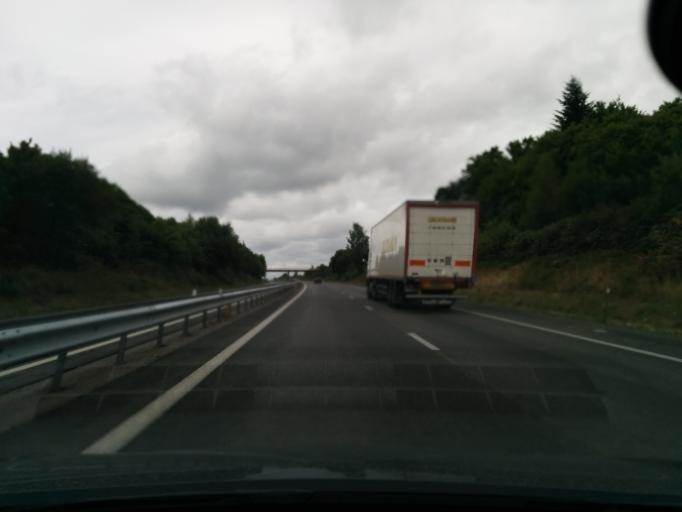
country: FR
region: Limousin
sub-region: Departement de la Haute-Vienne
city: Vicq-sur-Breuilh
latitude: 45.6403
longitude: 1.4200
